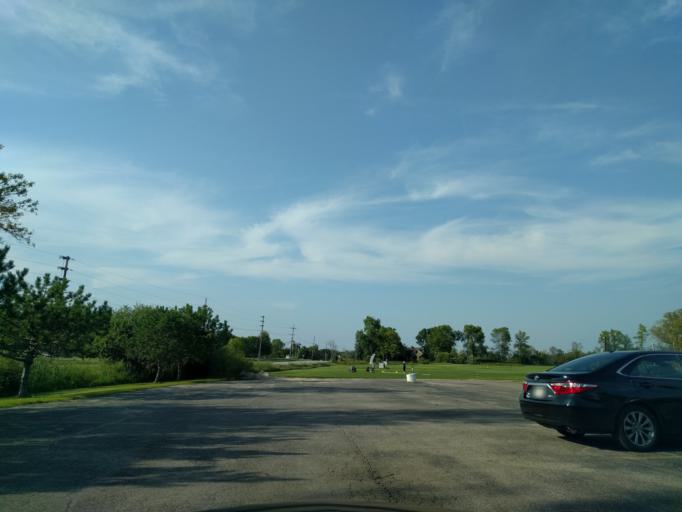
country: US
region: Wisconsin
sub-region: Ozaukee County
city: Thiensville
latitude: 43.2538
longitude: -87.9237
